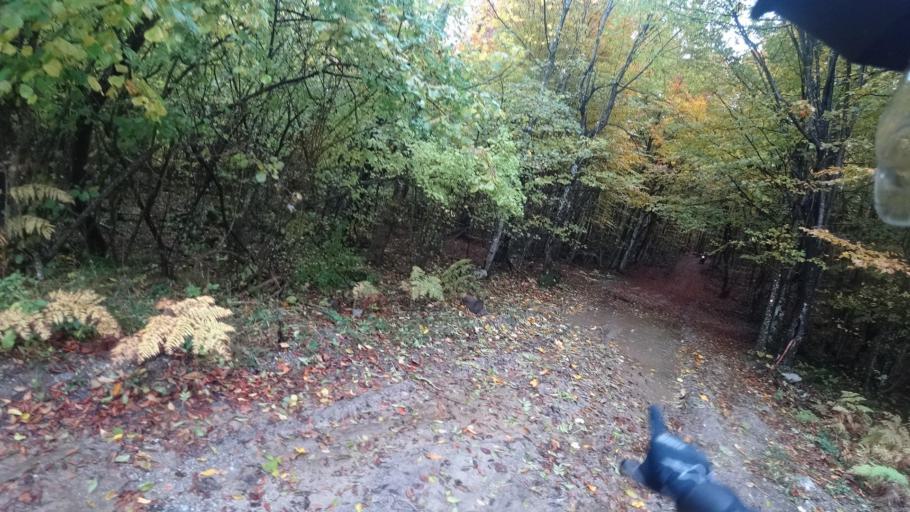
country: HR
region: Primorsko-Goranska
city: Vrbovsko
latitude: 45.4814
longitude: 15.0410
